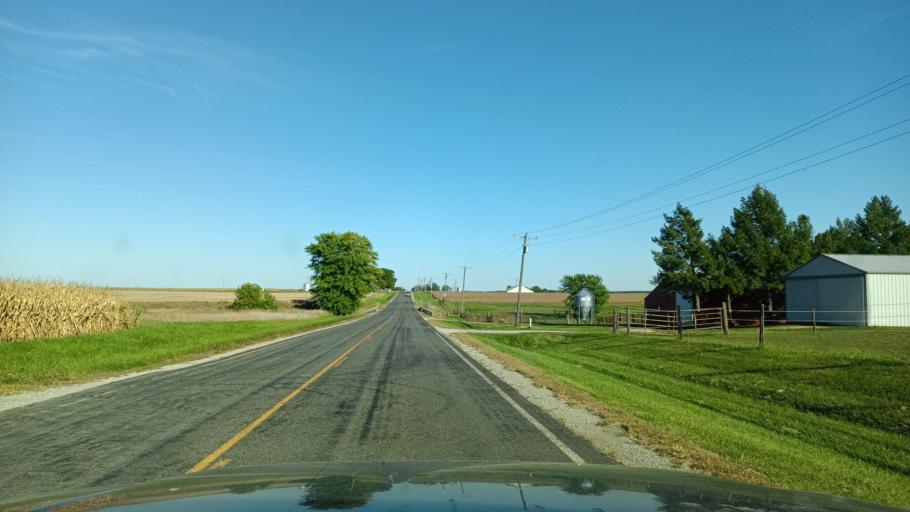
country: US
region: Illinois
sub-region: De Witt County
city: Farmer City
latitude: 40.2240
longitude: -88.7417
